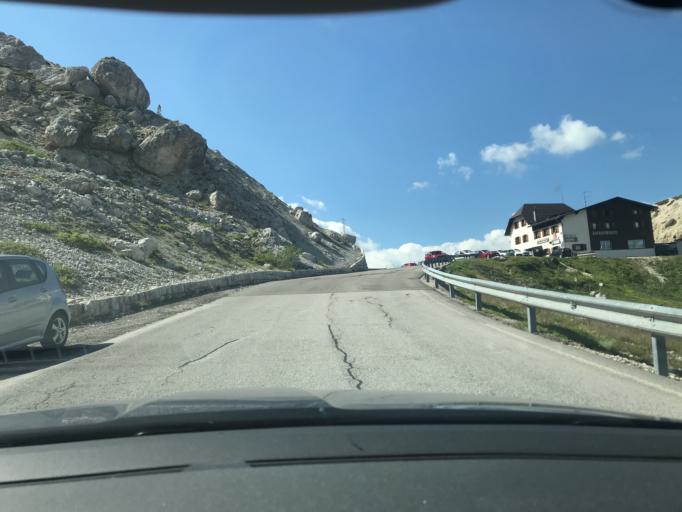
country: IT
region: Veneto
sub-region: Provincia di Belluno
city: Livinallongo del Col di Lana
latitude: 46.5325
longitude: 11.9891
